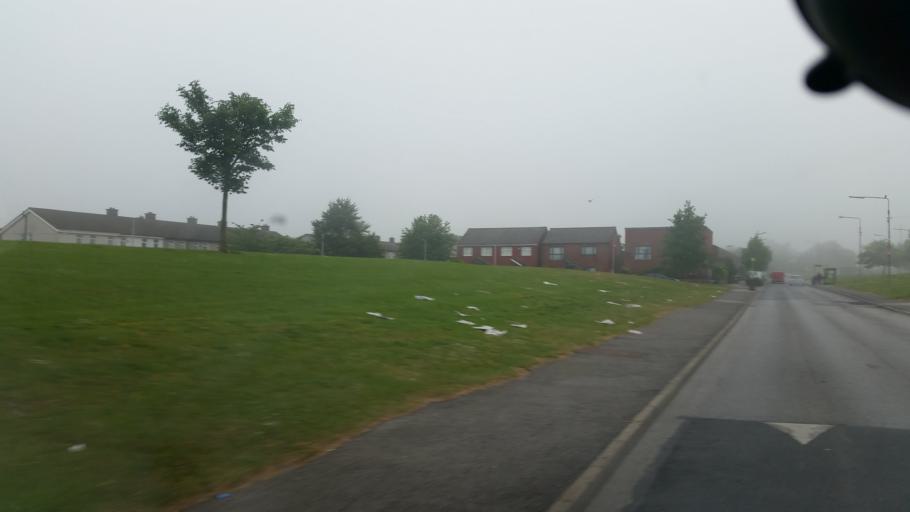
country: IE
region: Leinster
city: Ballymun
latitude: 53.4014
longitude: -6.2783
